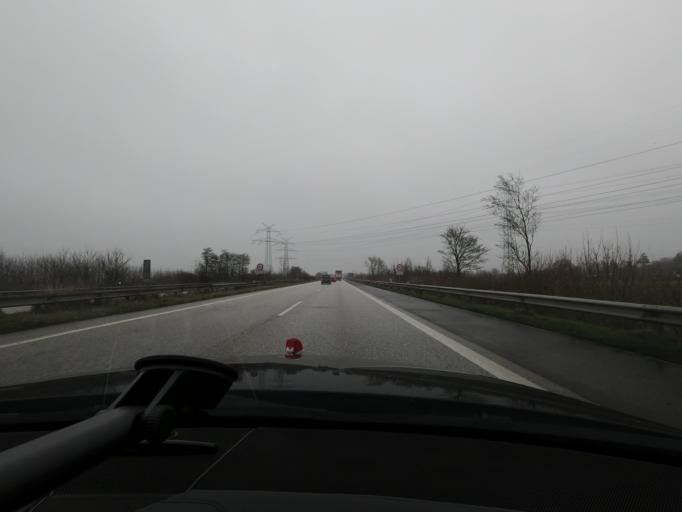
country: DE
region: Schleswig-Holstein
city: Borgstedt
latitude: 54.3435
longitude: 9.7065
